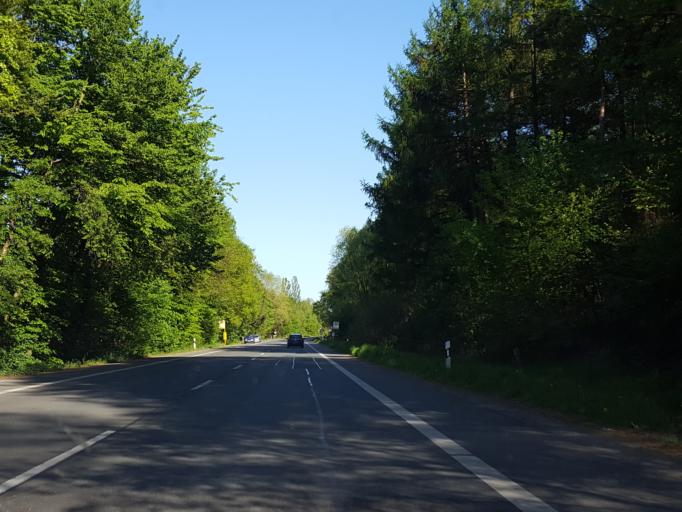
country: DE
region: North Rhine-Westphalia
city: Oer-Erkenschwick
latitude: 51.7144
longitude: 7.2737
